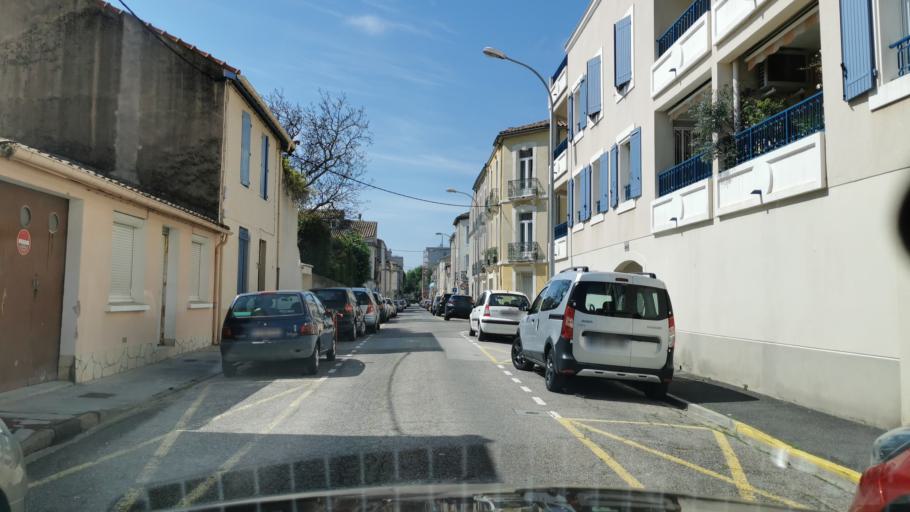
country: FR
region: Languedoc-Roussillon
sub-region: Departement de l'Aude
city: Narbonne
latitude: 43.1835
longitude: 3.0107
